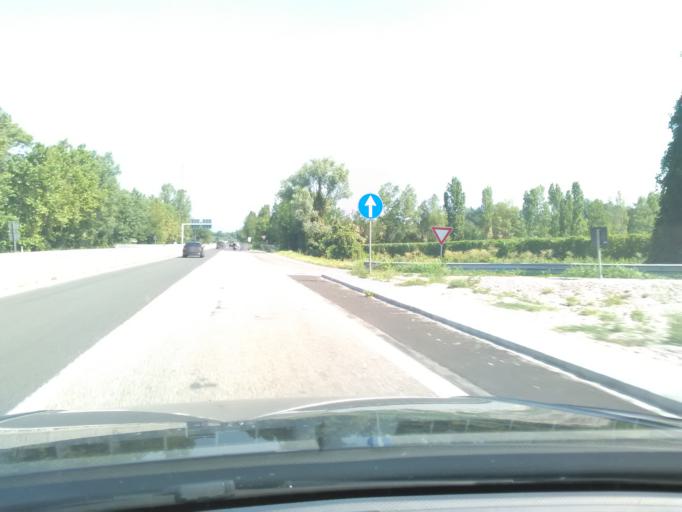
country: IT
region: Veneto
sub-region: Provincia di Verona
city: Cola
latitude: 45.4914
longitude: 10.7675
